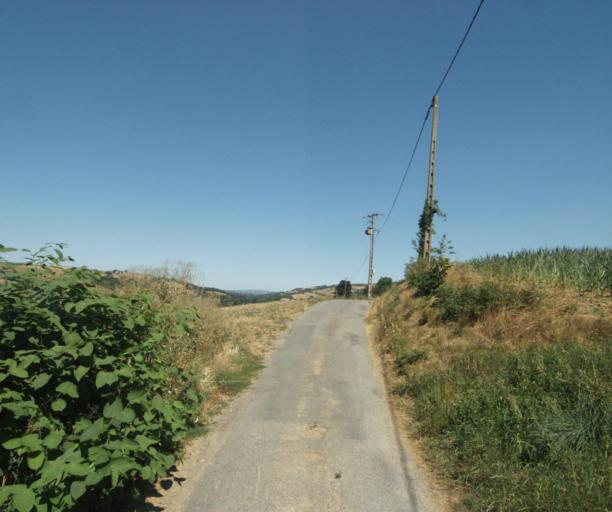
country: FR
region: Rhone-Alpes
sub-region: Departement du Rhone
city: Courzieu
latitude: 45.7499
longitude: 4.5534
